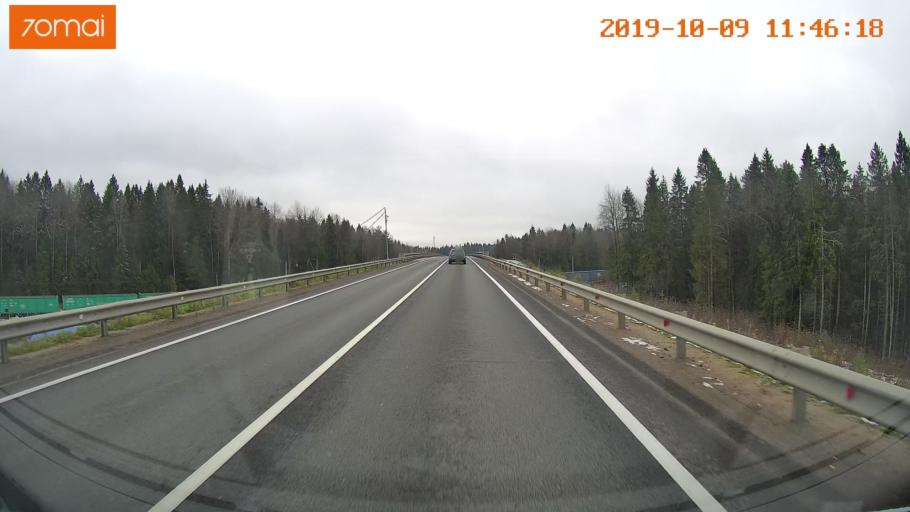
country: RU
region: Vologda
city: Gryazovets
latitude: 58.8552
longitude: 40.2011
